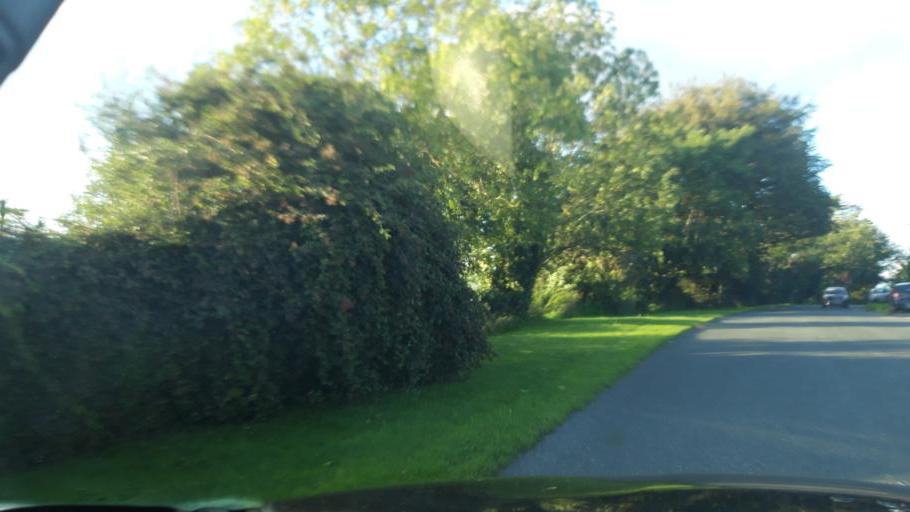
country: IE
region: Leinster
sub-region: An Iarmhi
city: Athlone
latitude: 53.4313
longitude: -7.8738
